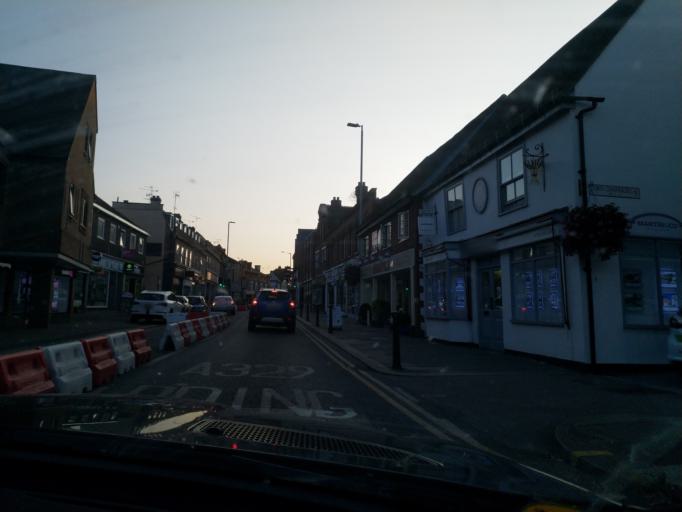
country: GB
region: England
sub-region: Kent
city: Sheerness
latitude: 51.4111
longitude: 0.8308
